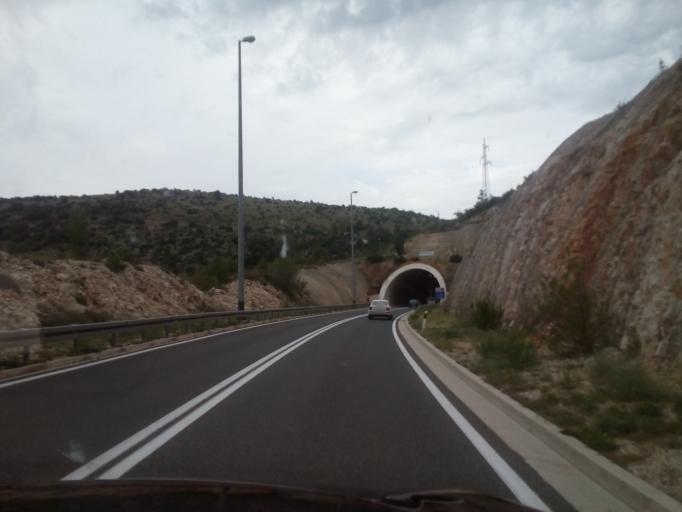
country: HR
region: Sibensko-Kniniska
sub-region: Grad Sibenik
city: Sibenik
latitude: 43.7678
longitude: 15.9378
